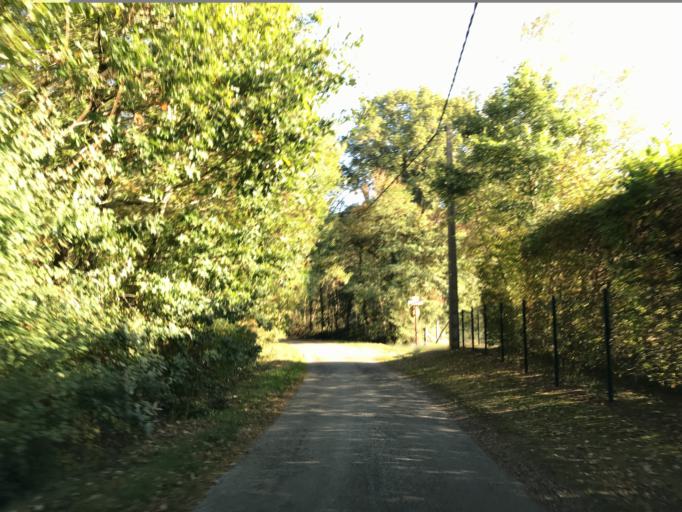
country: FR
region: Haute-Normandie
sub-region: Departement de l'Eure
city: Saint-Aubin-sur-Gaillon
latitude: 49.0747
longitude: 1.2688
